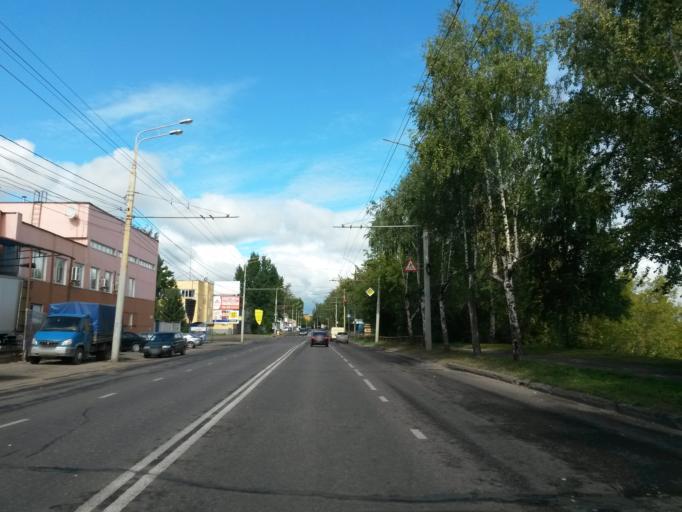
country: RU
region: Jaroslavl
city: Yaroslavl
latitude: 57.6580
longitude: 39.8645
